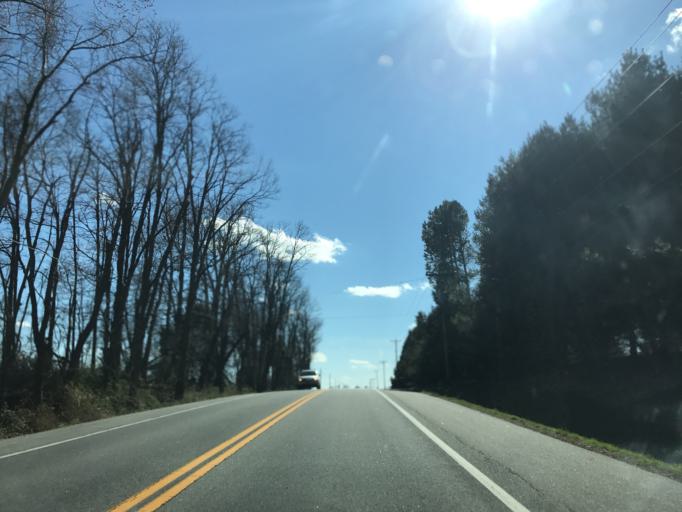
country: US
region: Maryland
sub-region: Kent County
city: Rock Hall
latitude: 39.1698
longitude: -76.1990
